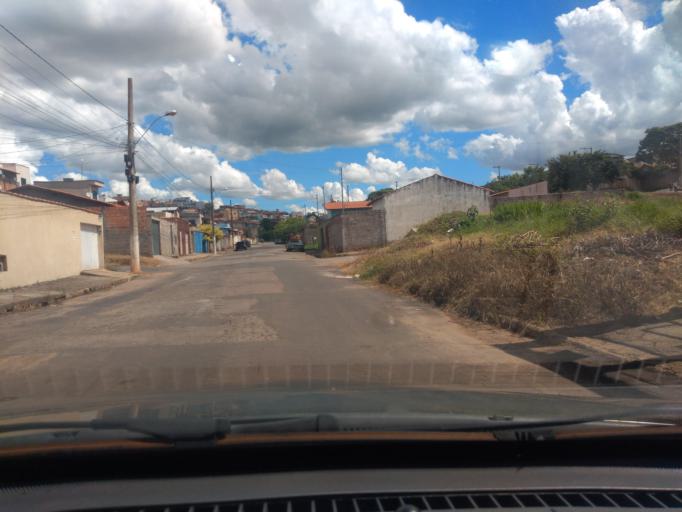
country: BR
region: Minas Gerais
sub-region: Tres Coracoes
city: Tres Coracoes
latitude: -21.6838
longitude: -45.2510
